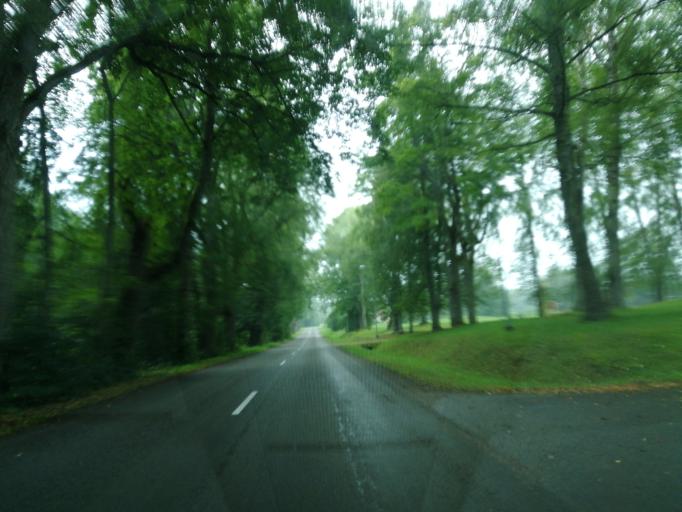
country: LV
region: Preilu Rajons
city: Jaunaglona
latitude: 56.2708
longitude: 27.0402
